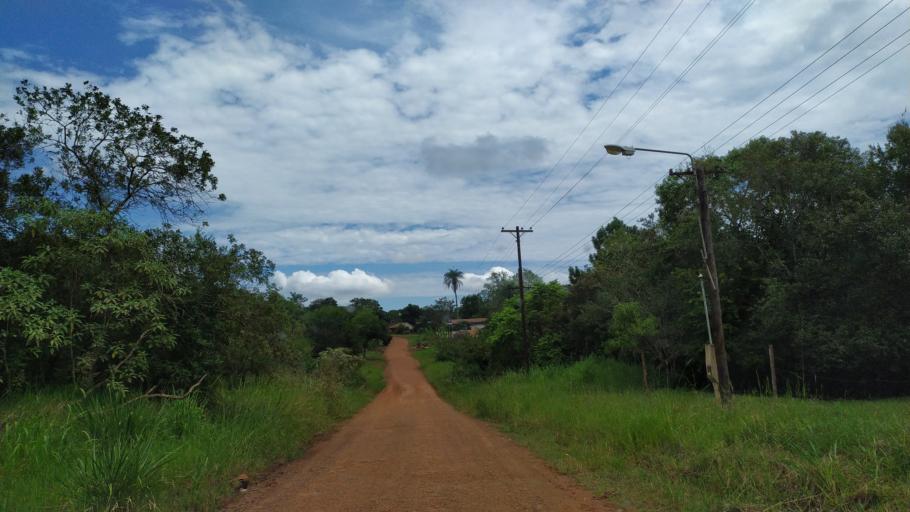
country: AR
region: Misiones
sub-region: Departamento de Eldorado
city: Eldorado
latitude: -26.5193
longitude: -54.5950
